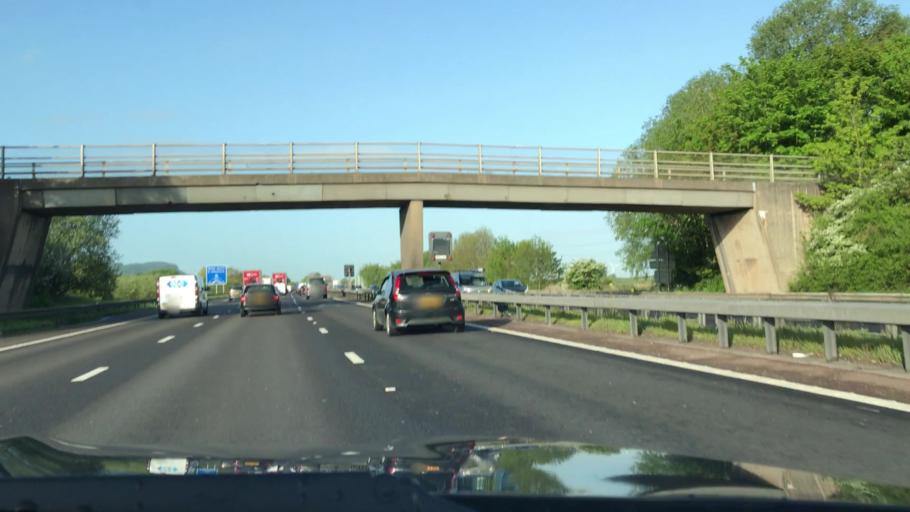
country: GB
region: England
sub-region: Cheshire West and Chester
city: Frodsham
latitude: 53.3024
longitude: -2.7212
